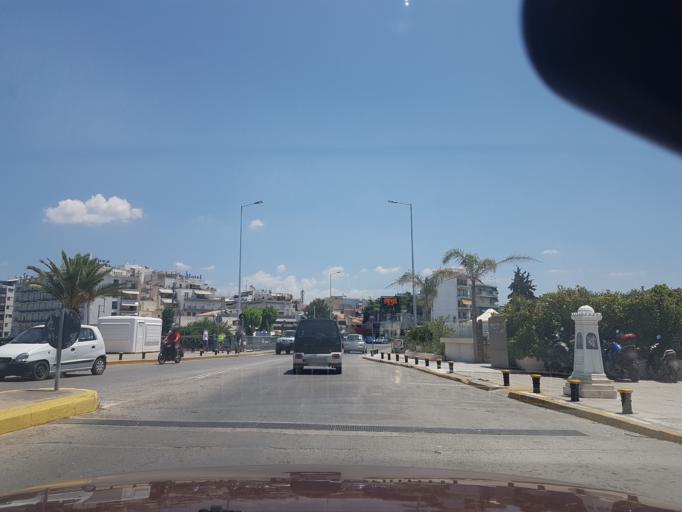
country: GR
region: Central Greece
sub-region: Nomos Evvoias
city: Chalkida
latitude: 38.4630
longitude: 23.5887
